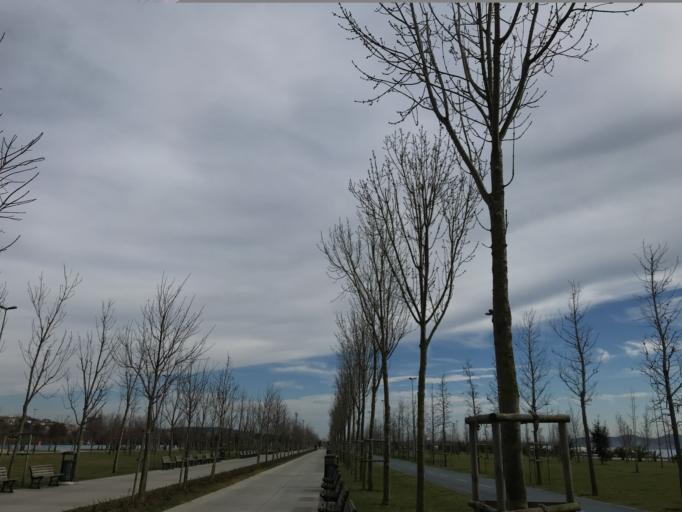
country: TR
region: Istanbul
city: Maltepe
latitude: 40.9343
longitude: 29.1119
